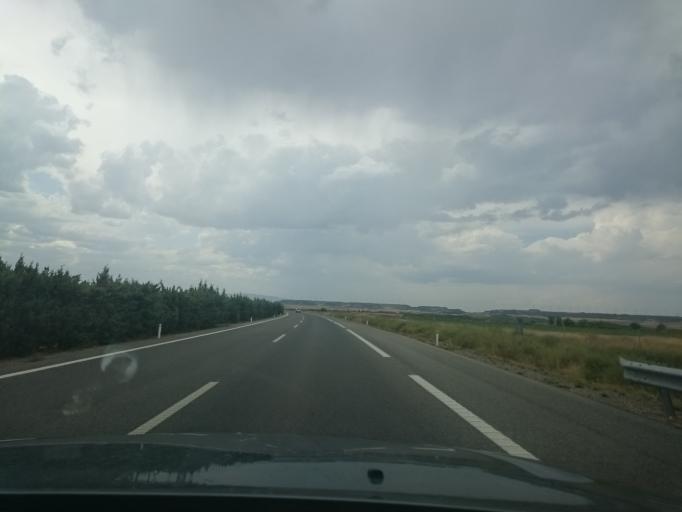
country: ES
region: Navarre
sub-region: Provincia de Navarra
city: Murchante
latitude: 42.0492
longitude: -1.6699
